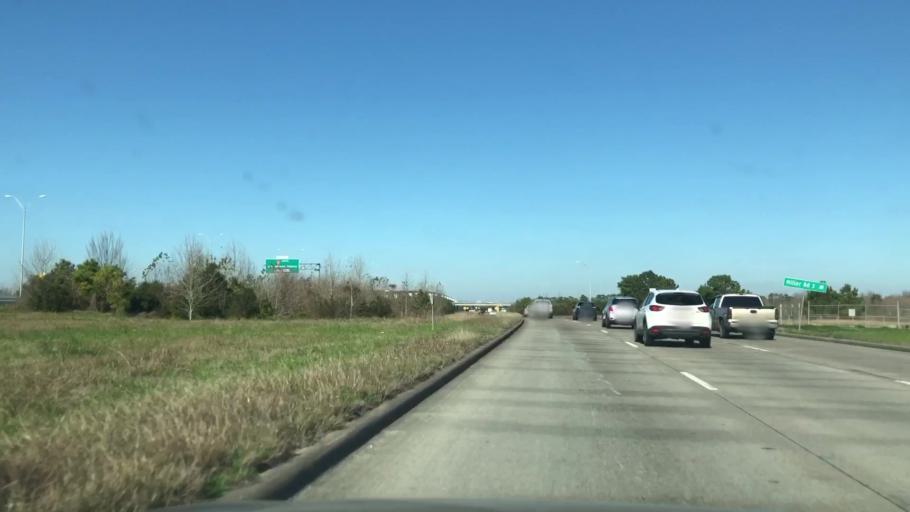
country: US
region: Texas
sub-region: Harris County
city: Cloverleaf
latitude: 29.8282
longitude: -95.1706
